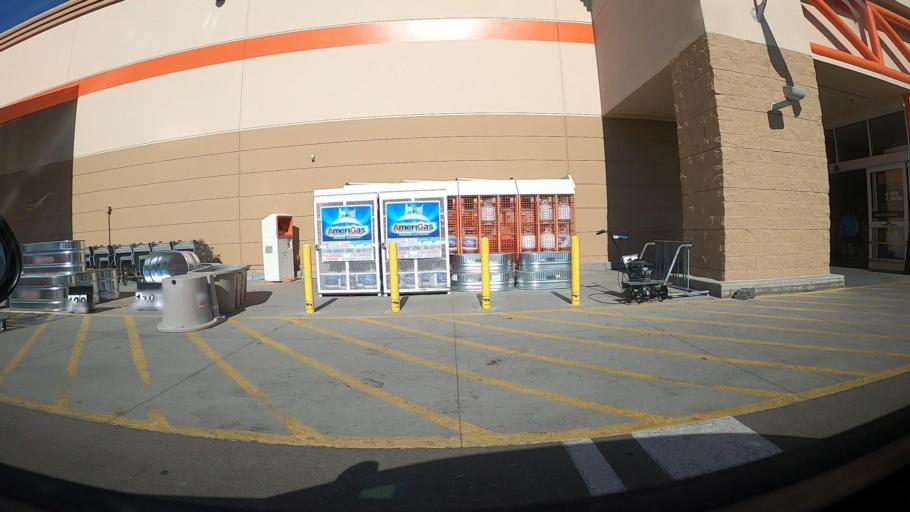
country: US
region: Idaho
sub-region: Ada County
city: Meridian
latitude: 43.5947
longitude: -116.3900
